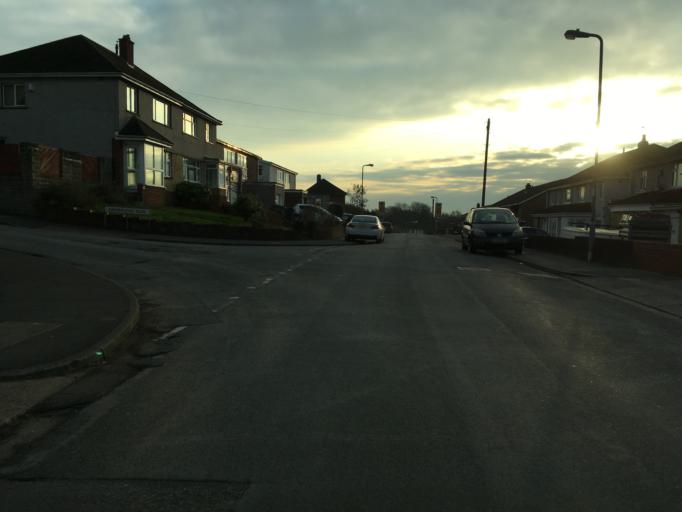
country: GB
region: Wales
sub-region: Cardiff
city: Cardiff
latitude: 51.5124
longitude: -3.1349
